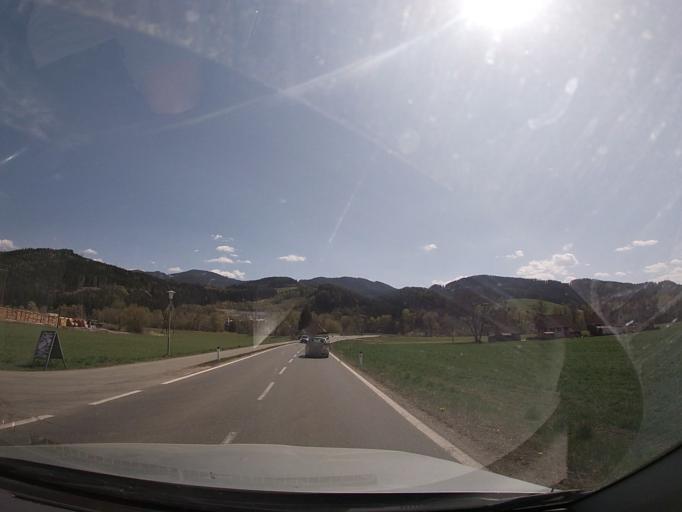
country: AT
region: Styria
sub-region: Politischer Bezirk Murtal
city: Apfelberg
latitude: 47.2017
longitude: 14.8352
